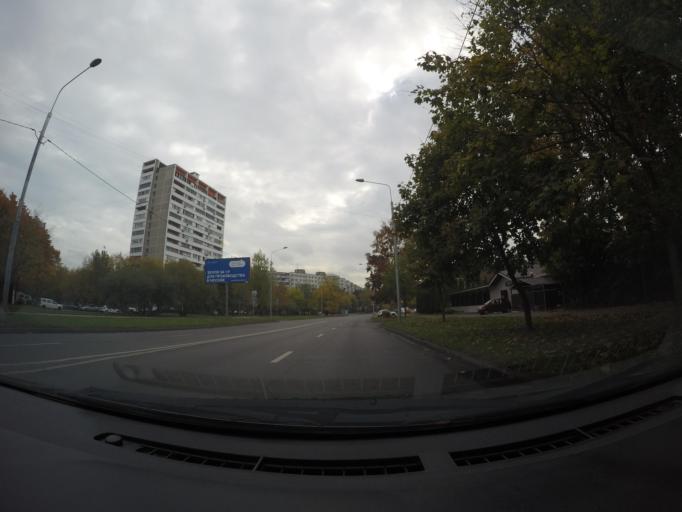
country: RU
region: Moscow
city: Ivanovskoye
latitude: 55.7664
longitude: 37.8223
